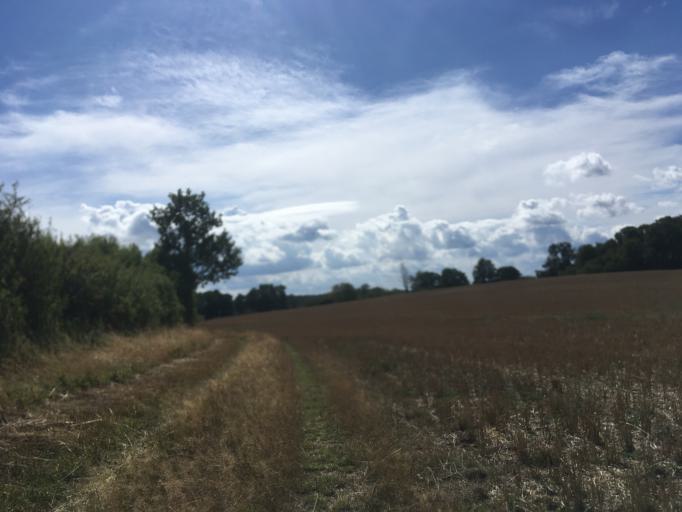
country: DE
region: Brandenburg
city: Gerswalde
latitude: 53.1382
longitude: 13.7809
